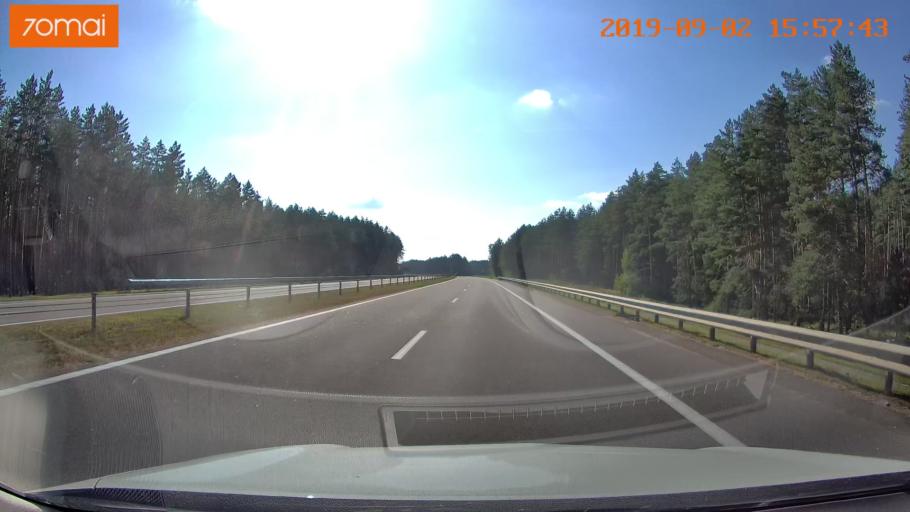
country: BY
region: Minsk
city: Byerazino
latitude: 53.8353
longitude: 29.0312
